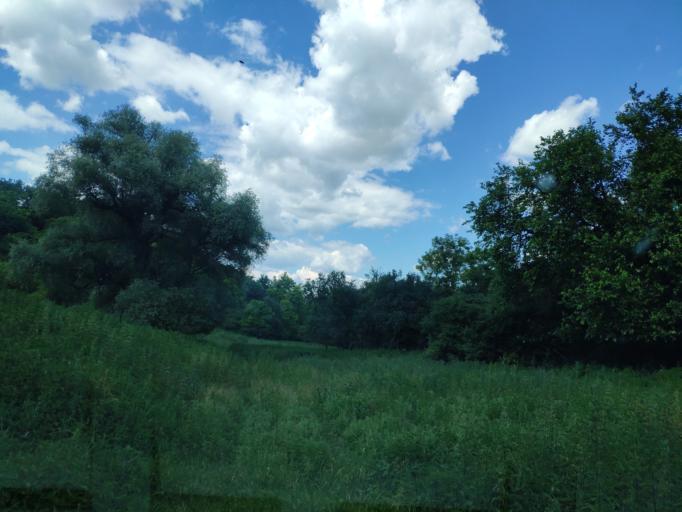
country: HU
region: Borsod-Abauj-Zemplen
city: Arlo
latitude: 48.2551
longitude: 20.1688
